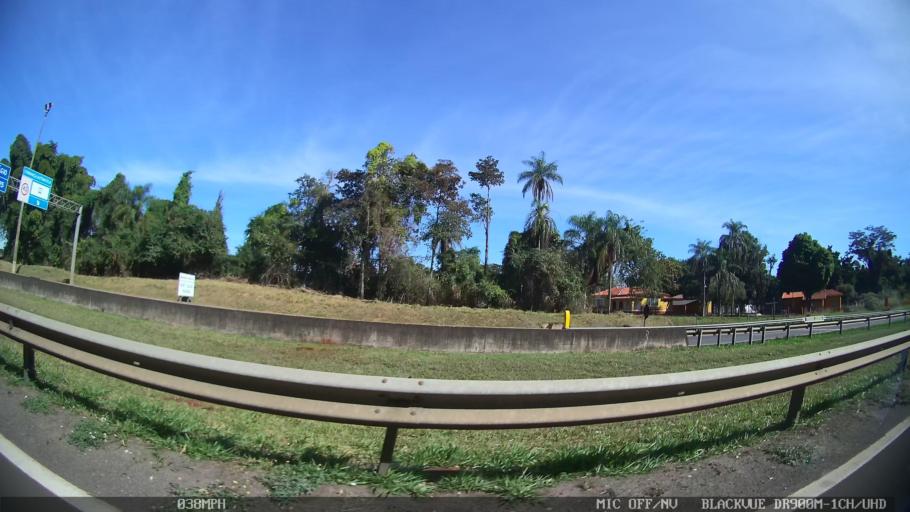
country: BR
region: Sao Paulo
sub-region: Pirassununga
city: Pirassununga
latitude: -21.9549
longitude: -47.4605
